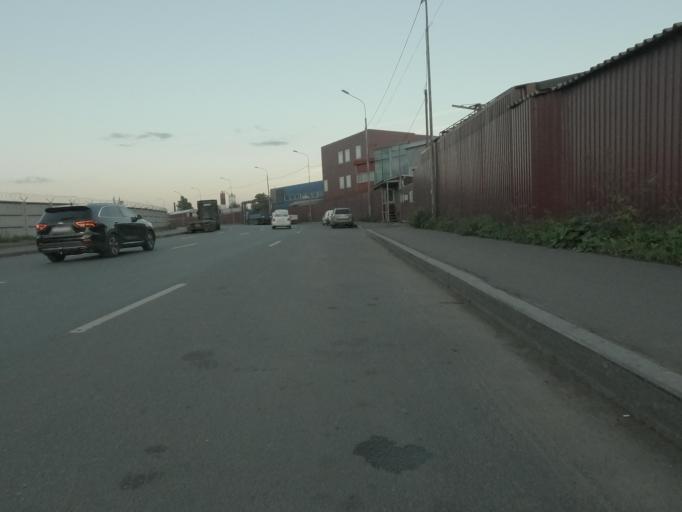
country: RU
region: St.-Petersburg
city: Vasyl'evsky Ostrov
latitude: 59.9036
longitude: 30.2370
